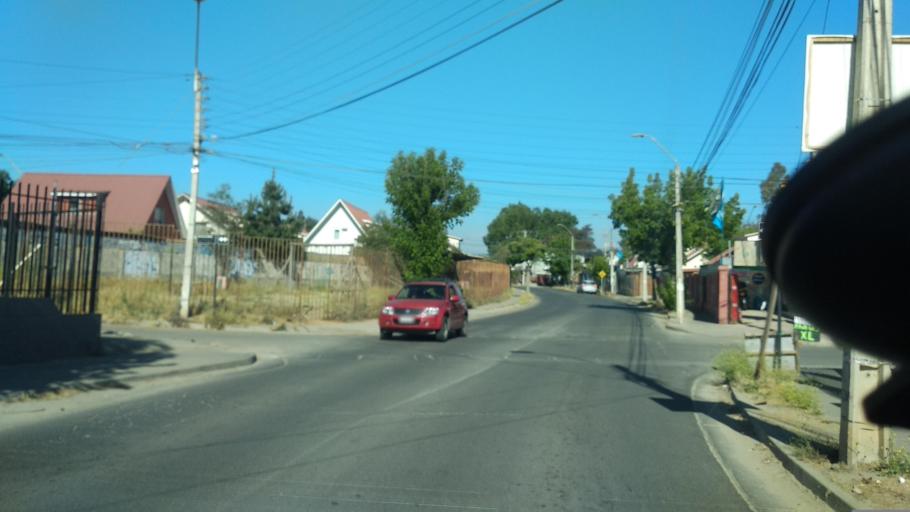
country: CL
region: Valparaiso
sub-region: Provincia de Marga Marga
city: Villa Alemana
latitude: -33.0387
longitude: -71.3890
